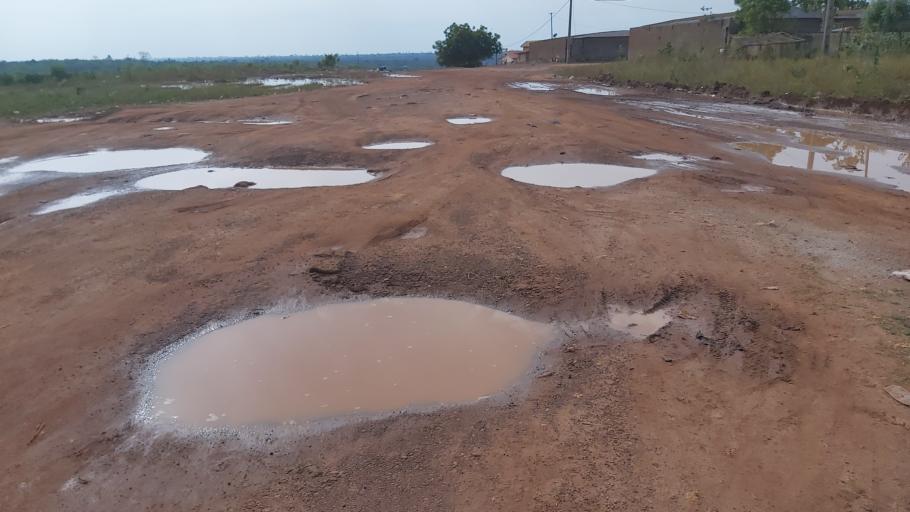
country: CI
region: Lacs
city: Yamoussoukro
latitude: 6.7853
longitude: -5.2780
